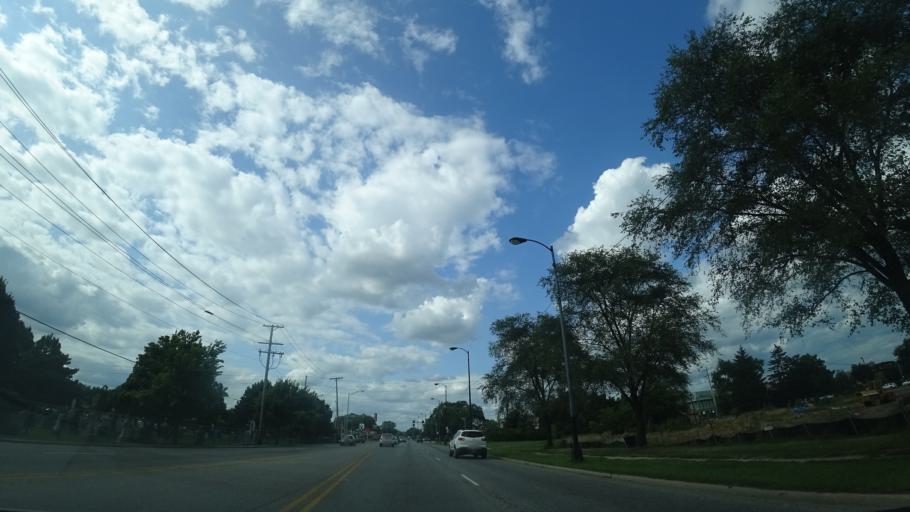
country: US
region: Illinois
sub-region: Cook County
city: Merrionette Park
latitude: 41.6903
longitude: -87.7201
